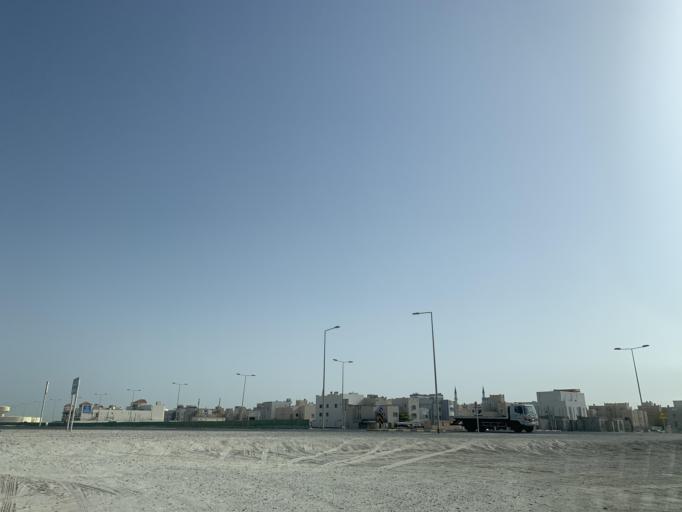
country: BH
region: Muharraq
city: Al Muharraq
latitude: 26.2727
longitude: 50.5940
